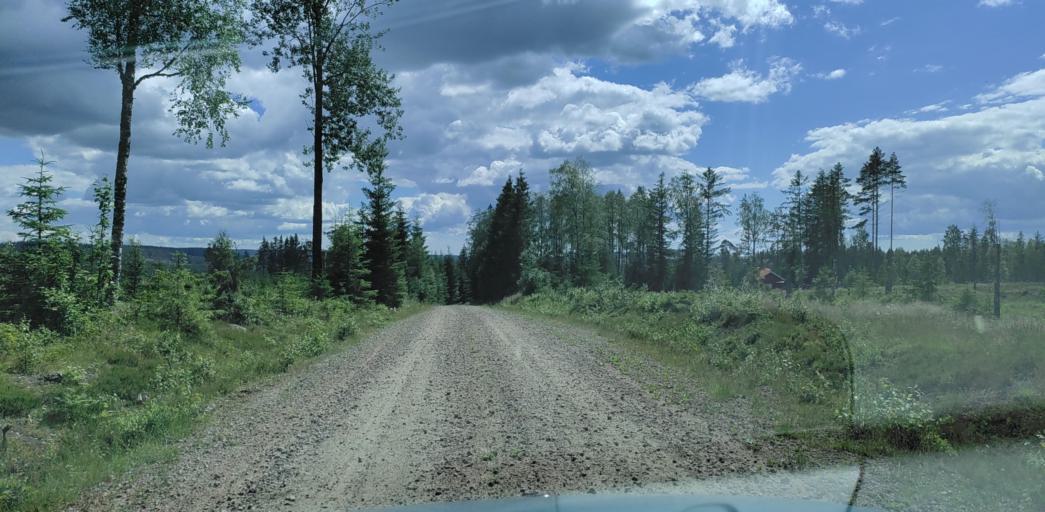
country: SE
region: Vaermland
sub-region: Hagfors Kommun
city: Ekshaerad
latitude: 60.0495
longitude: 13.3093
